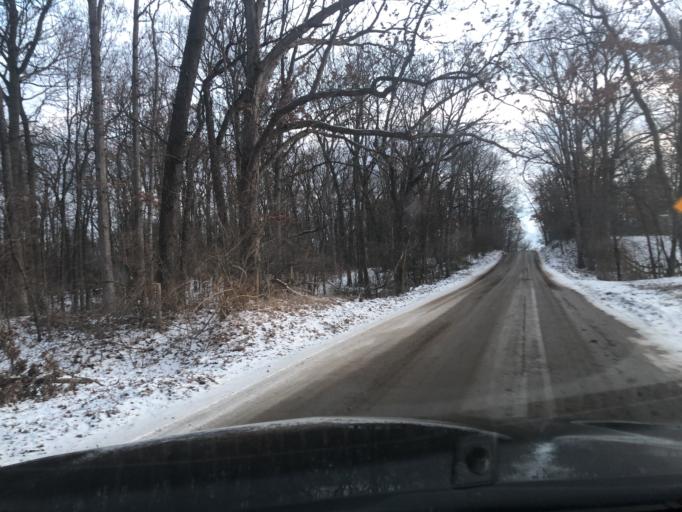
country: US
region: Michigan
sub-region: Oakland County
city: Milford
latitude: 42.5706
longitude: -83.6389
